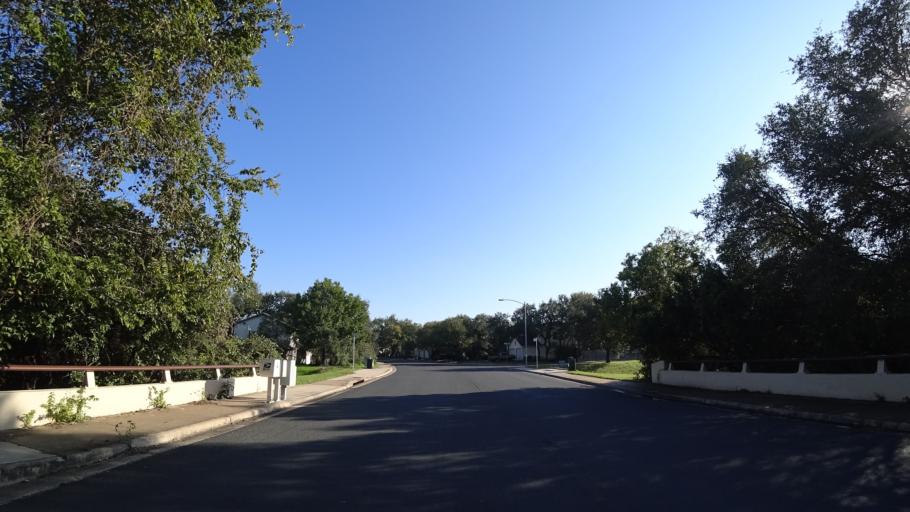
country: US
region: Texas
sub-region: Travis County
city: Shady Hollow
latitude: 30.2080
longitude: -97.8466
